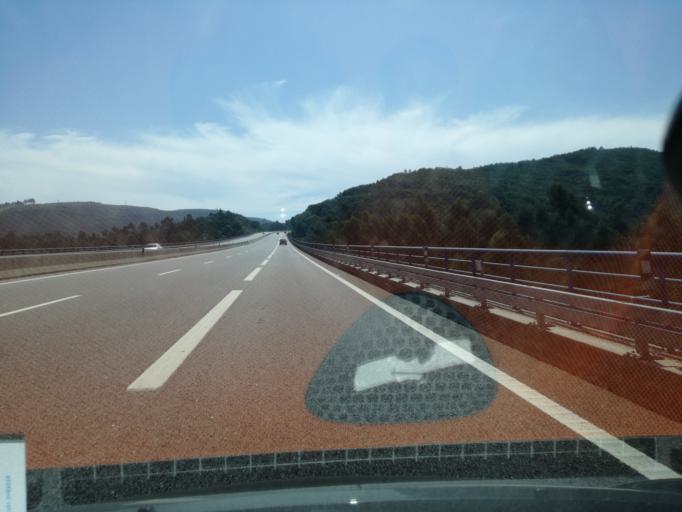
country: PT
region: Viana do Castelo
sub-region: Caminha
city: Vila Praia de Ancora
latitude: 41.8001
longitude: -8.7988
